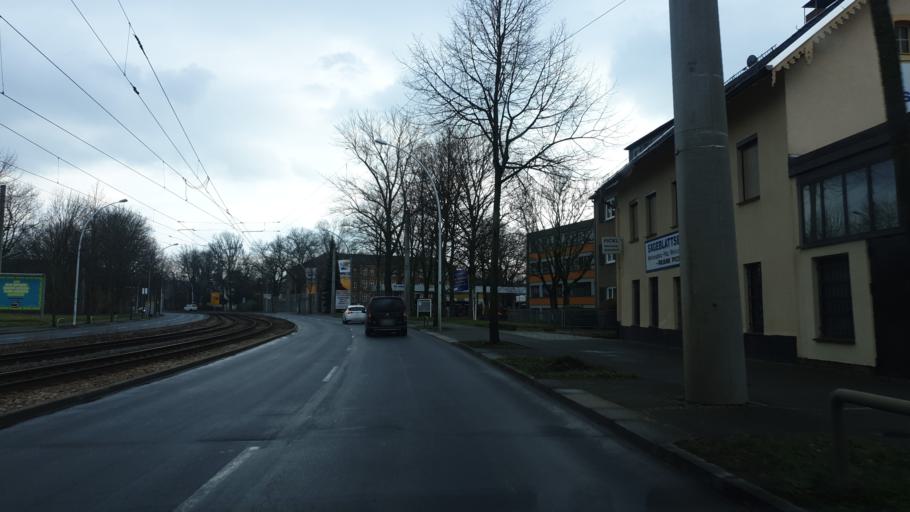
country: DE
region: Saxony
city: Chemnitz
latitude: 50.8015
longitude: 12.9110
